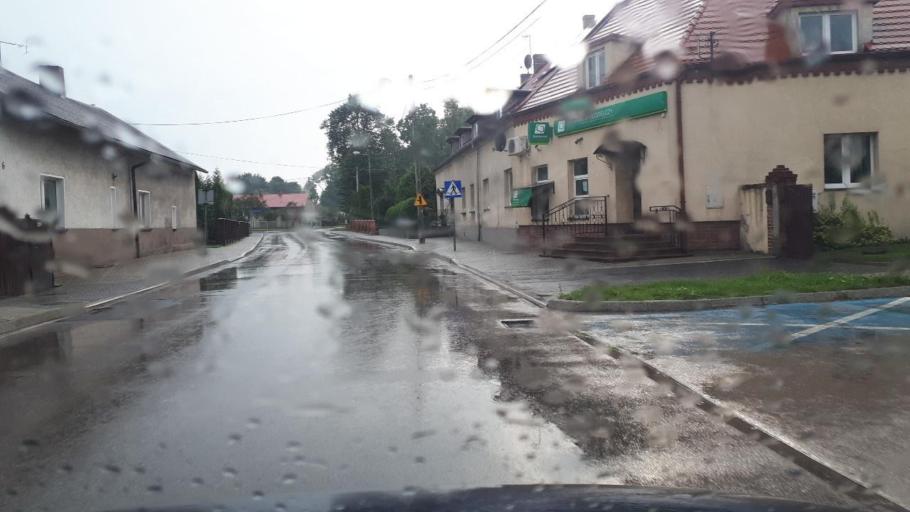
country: PL
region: Silesian Voivodeship
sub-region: Powiat gliwicki
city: Wielowies
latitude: 50.5062
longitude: 18.6095
